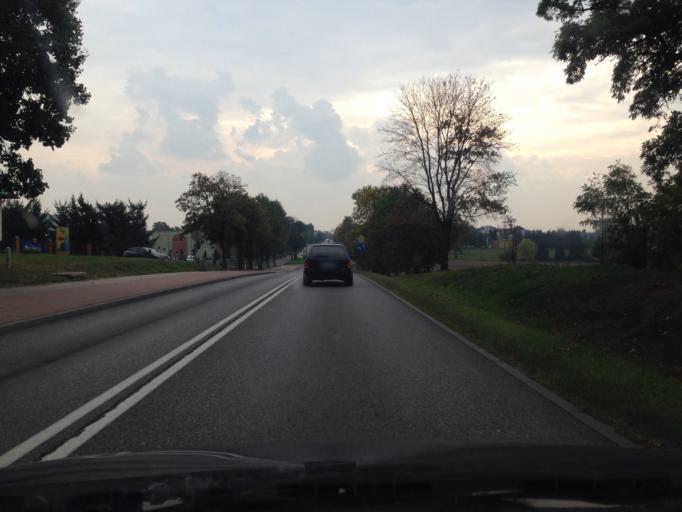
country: PL
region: Pomeranian Voivodeship
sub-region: Powiat sztumski
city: Sztum
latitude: 53.9313
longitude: 19.0277
